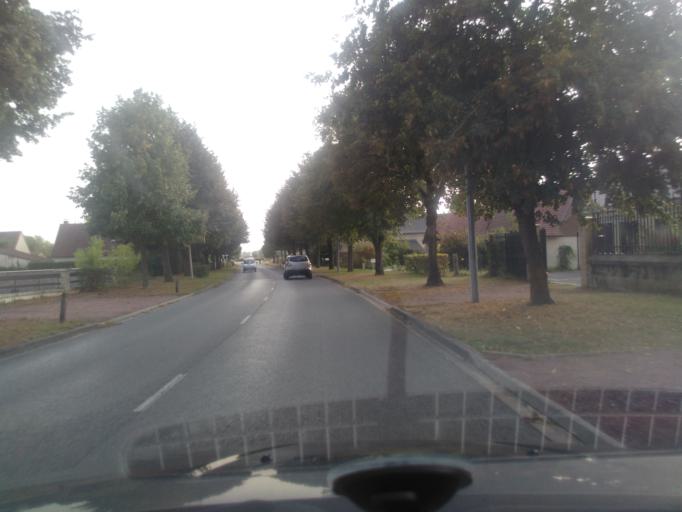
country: FR
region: Picardie
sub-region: Departement de l'Aisne
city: Laon
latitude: 49.5508
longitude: 3.6034
